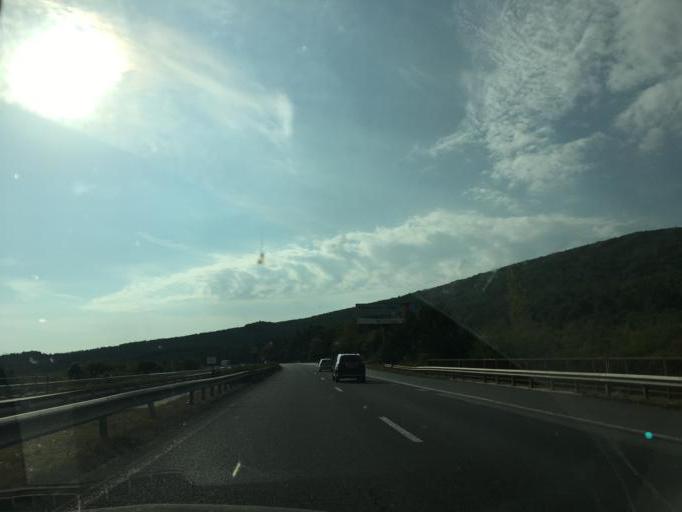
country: BG
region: Sofiya
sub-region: Obshtina Elin Pelin
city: Elin Pelin
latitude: 42.6000
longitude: 23.5663
